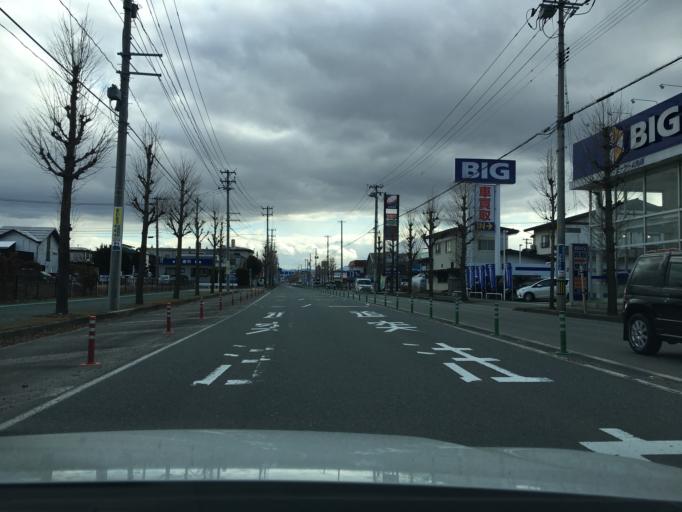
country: JP
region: Yamagata
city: Yamagata-shi
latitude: 38.2466
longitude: 140.3086
